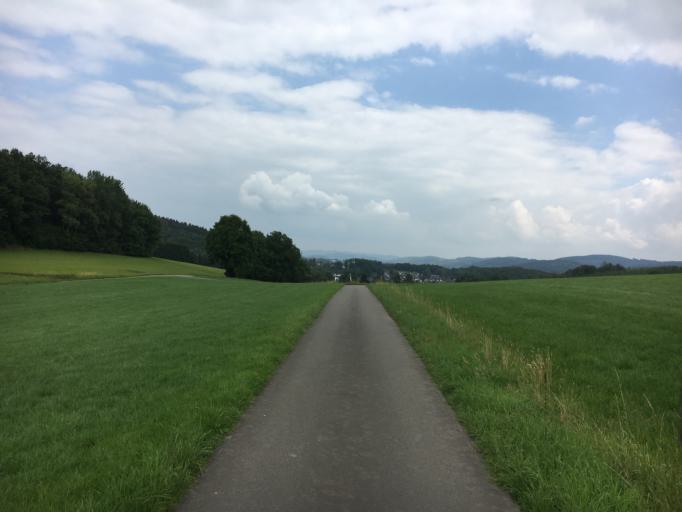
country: DE
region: North Rhine-Westphalia
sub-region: Regierungsbezirk Arnsberg
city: Attendorn
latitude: 51.1072
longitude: 7.8512
